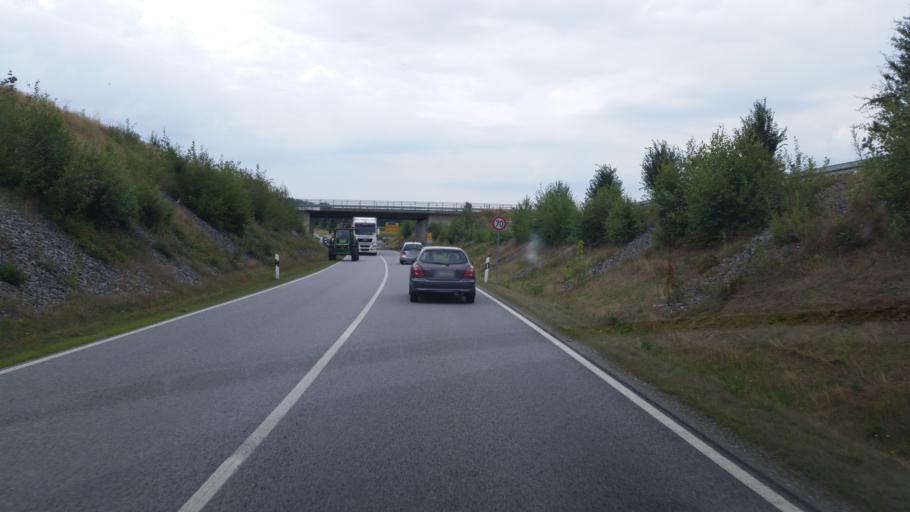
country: DE
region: Saxony
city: Elstra
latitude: 51.2268
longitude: 14.1472
